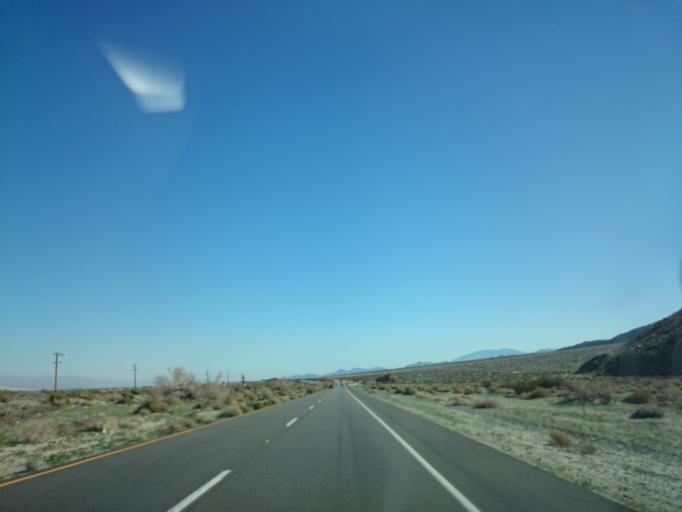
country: US
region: California
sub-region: Riverside County
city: Garnet
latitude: 33.8726
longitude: -116.5810
